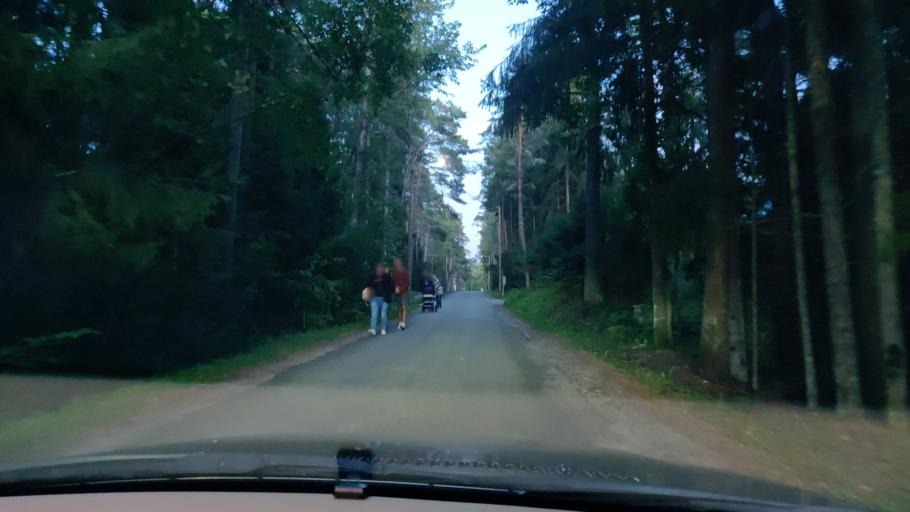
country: EE
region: Harju
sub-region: Keila linn
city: Keila
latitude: 59.3462
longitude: 24.2632
